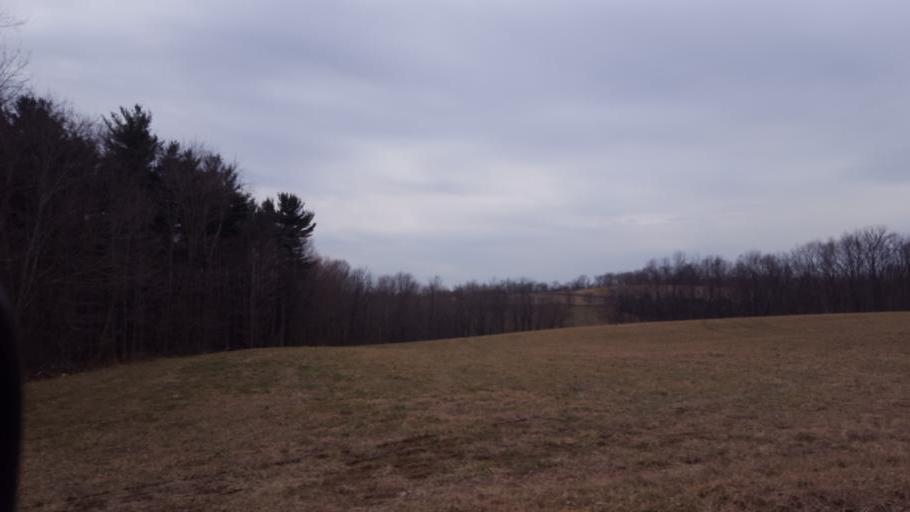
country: US
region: Ohio
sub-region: Ashland County
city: Loudonville
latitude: 40.6941
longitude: -82.2552
